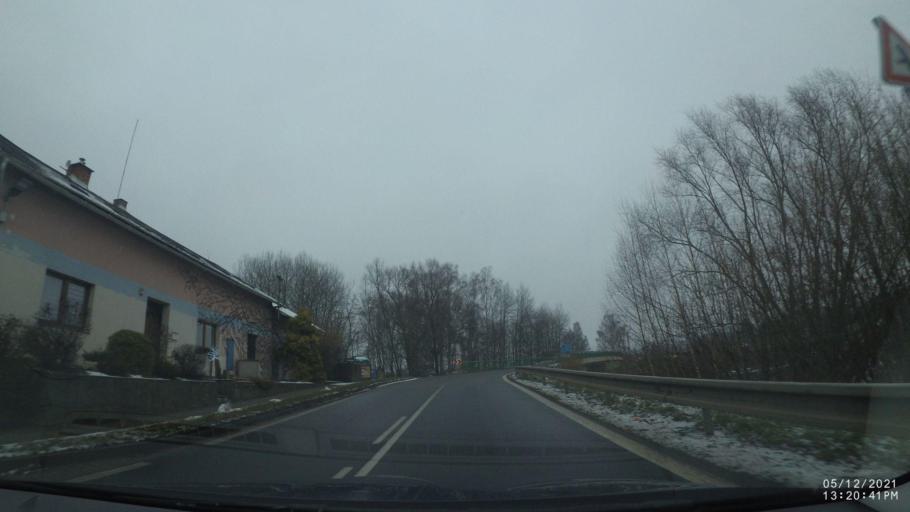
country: CZ
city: Velke Porici
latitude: 50.4523
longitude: 16.1883
